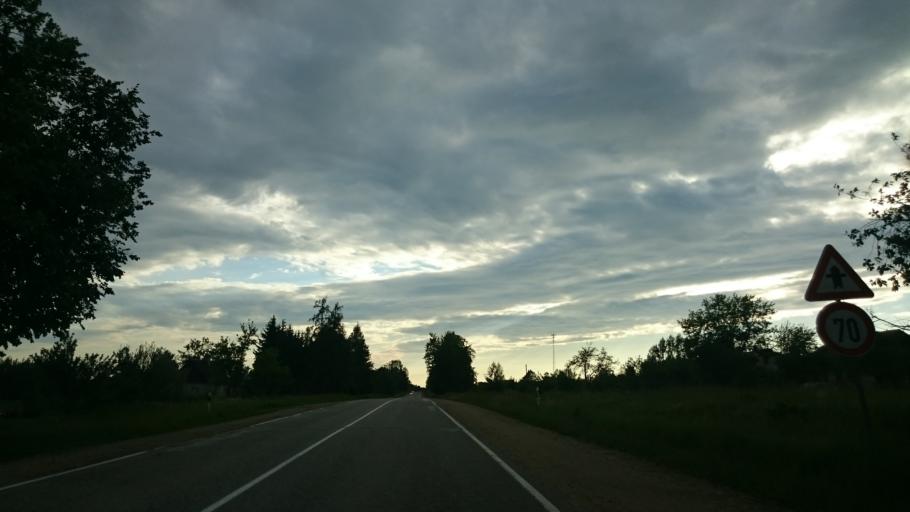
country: LV
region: Ludzas Rajons
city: Ludza
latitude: 56.5378
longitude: 27.6374
